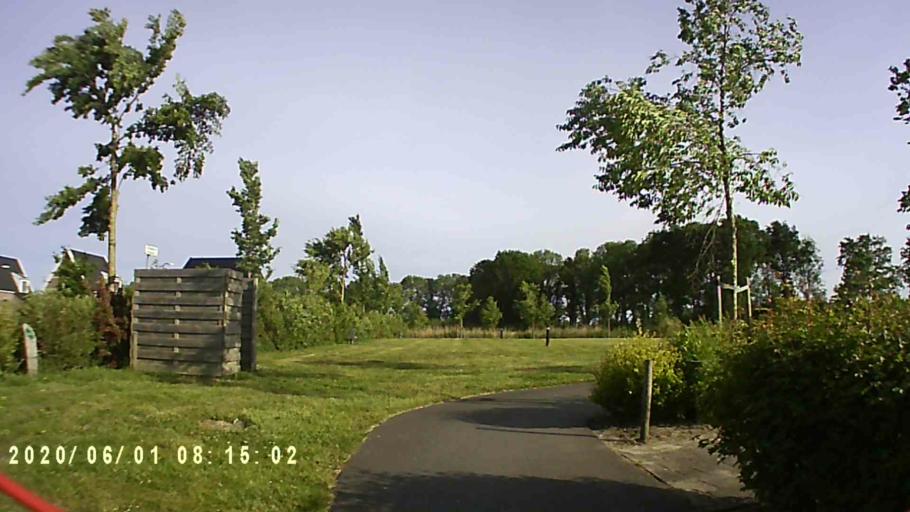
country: NL
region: Friesland
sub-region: Gemeente Ferwerderadiel
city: Burdaard
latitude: 53.2967
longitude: 5.8815
